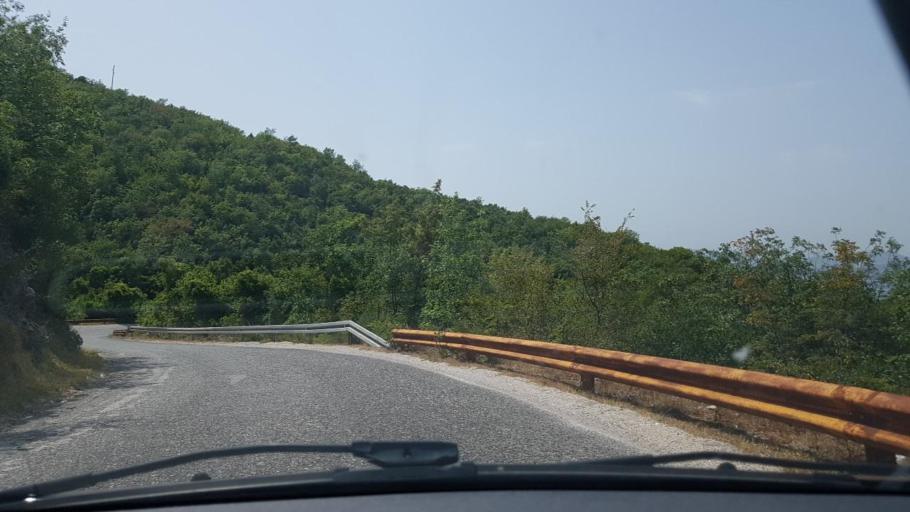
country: BA
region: Federation of Bosnia and Herzegovina
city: Tasovcici
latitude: 43.0156
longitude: 17.7846
